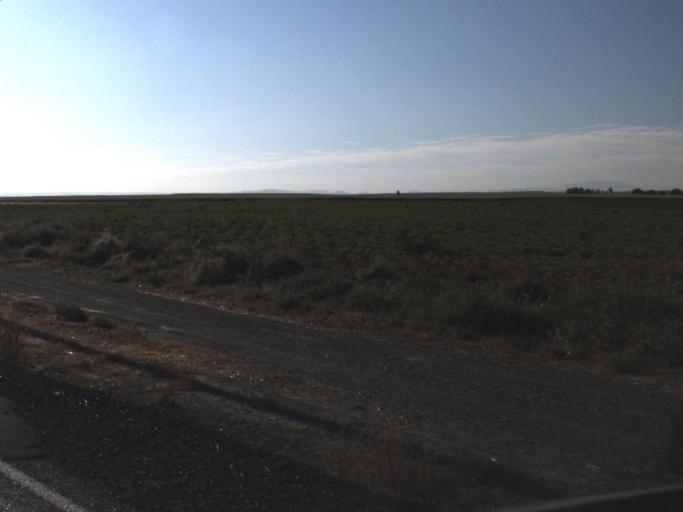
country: US
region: Washington
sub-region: Walla Walla County
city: Burbank
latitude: 46.2519
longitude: -118.8071
